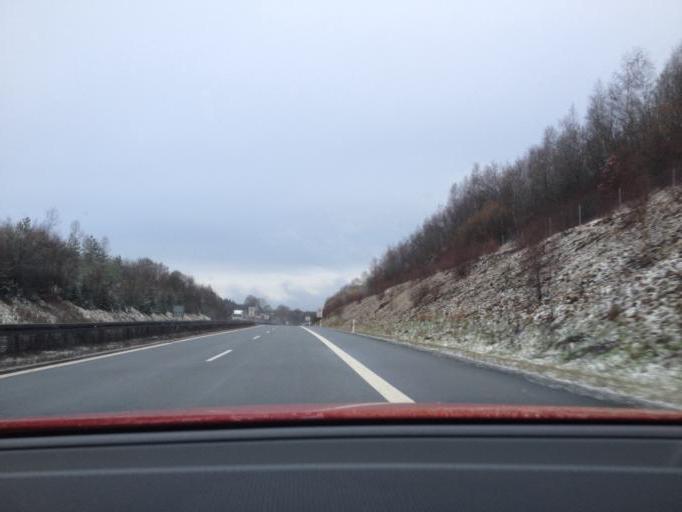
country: DE
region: Bavaria
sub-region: Upper Franconia
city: Selb
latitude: 50.1873
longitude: 12.1135
